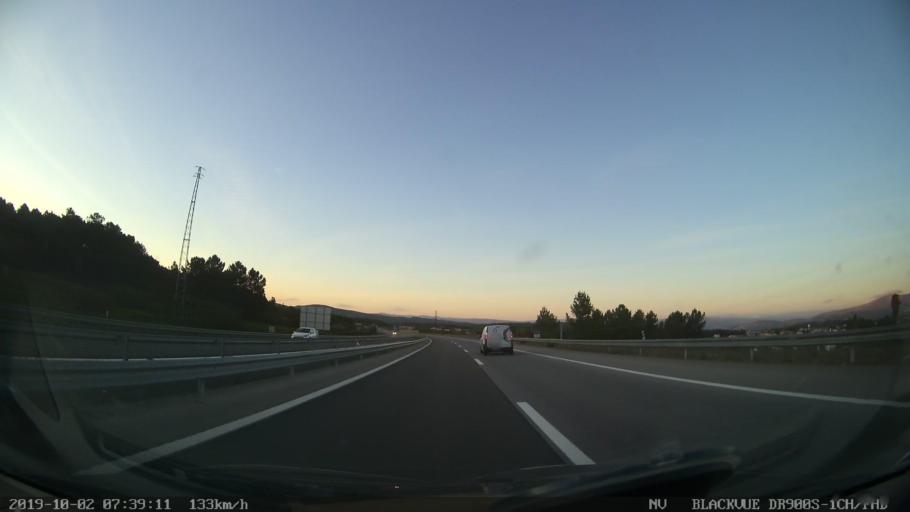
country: PT
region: Vila Real
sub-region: Vila Real
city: Vila Real
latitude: 41.2848
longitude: -7.6913
